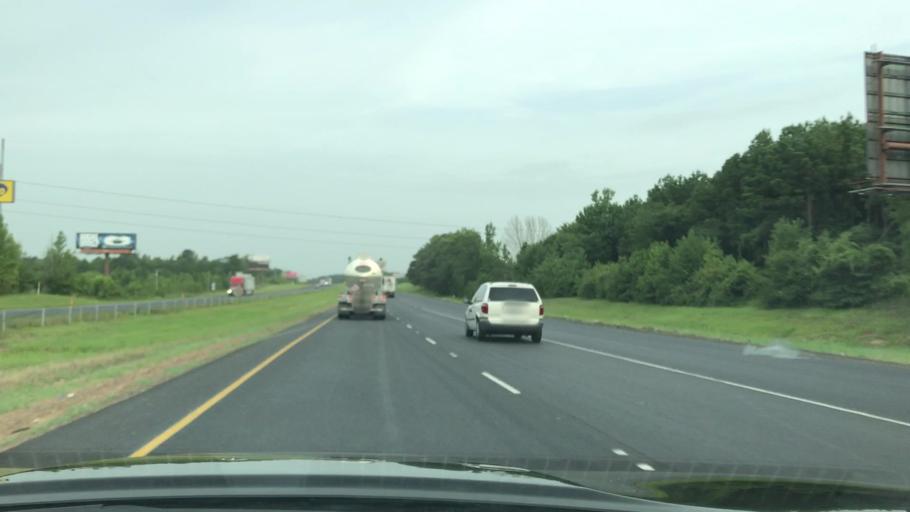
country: US
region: Louisiana
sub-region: Caddo Parish
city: Greenwood
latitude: 32.4479
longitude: -93.9833
